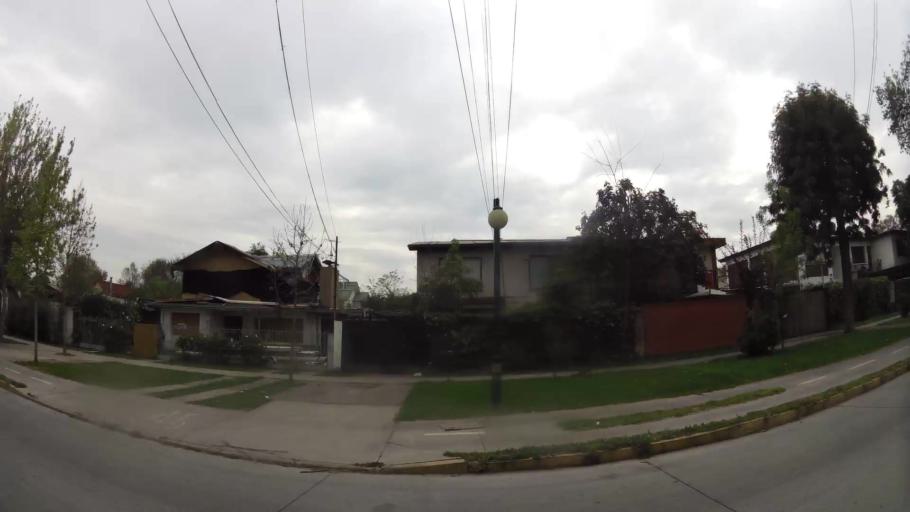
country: CL
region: Santiago Metropolitan
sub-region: Provincia de Santiago
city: Villa Presidente Frei, Nunoa, Santiago, Chile
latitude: -33.4628
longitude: -70.5877
